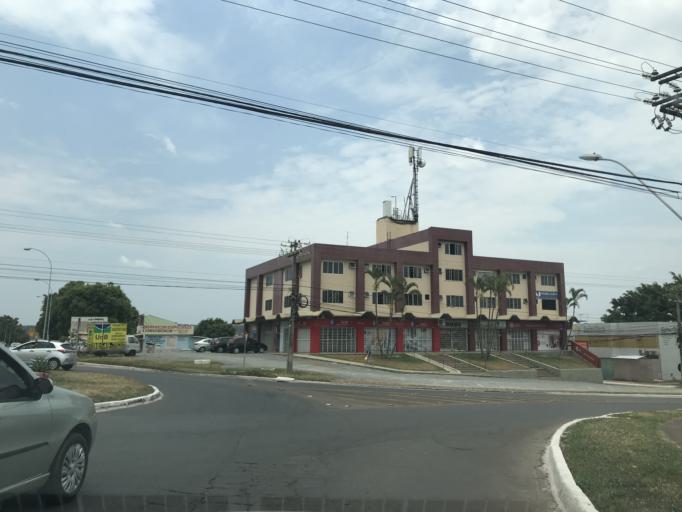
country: BR
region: Federal District
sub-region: Brasilia
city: Brasilia
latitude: -15.6561
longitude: -47.8051
